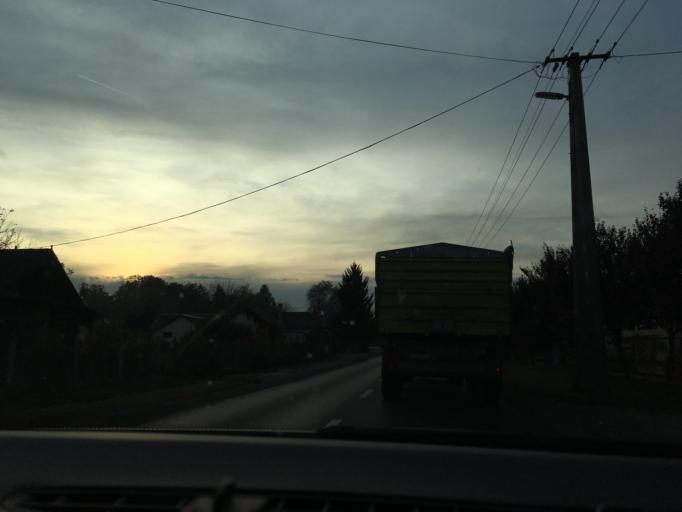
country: HU
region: Szabolcs-Szatmar-Bereg
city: Kallosemjen
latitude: 47.8591
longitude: 21.9377
